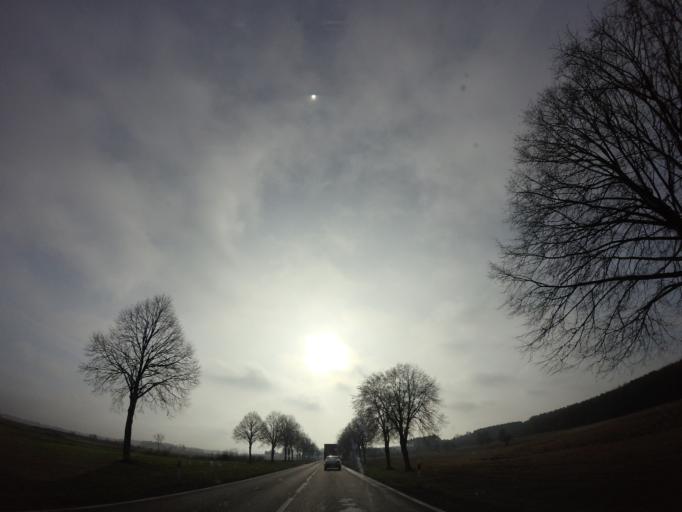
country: PL
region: West Pomeranian Voivodeship
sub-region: Powiat walecki
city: Walcz
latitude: 53.3238
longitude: 16.3113
